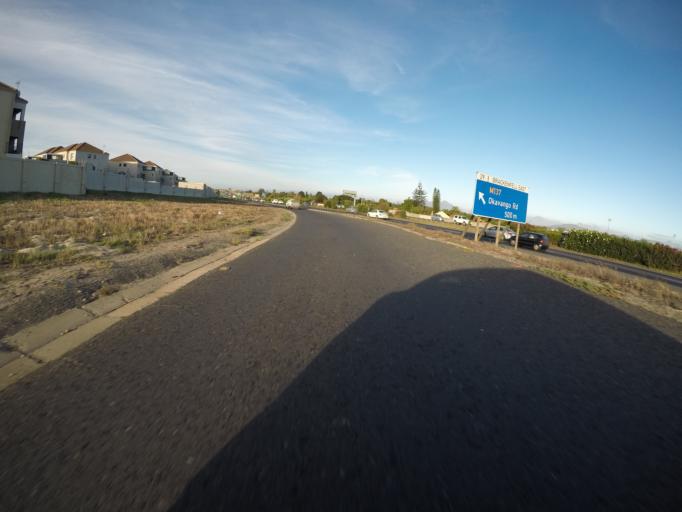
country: ZA
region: Western Cape
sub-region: City of Cape Town
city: Kraaifontein
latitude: -33.8640
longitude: 18.6855
